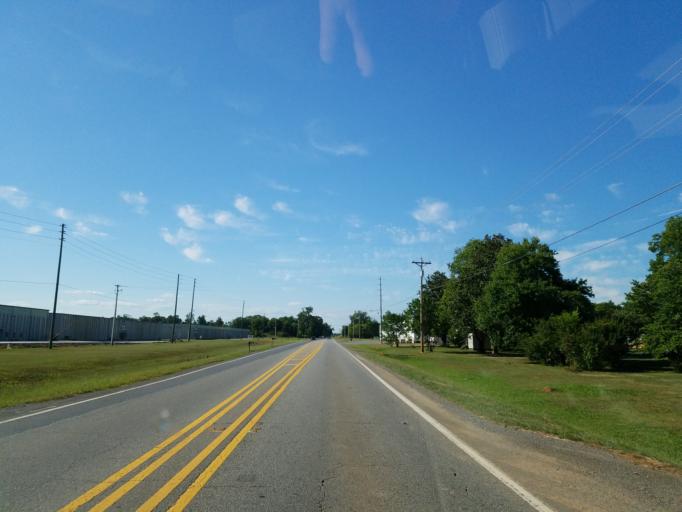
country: US
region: Georgia
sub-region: Bartow County
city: Adairsville
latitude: 34.4349
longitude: -84.9350
